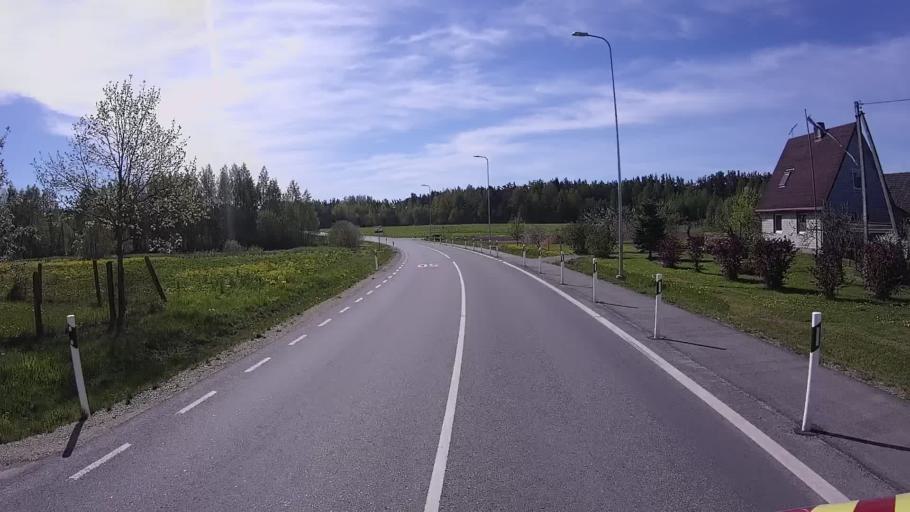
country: EE
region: Polvamaa
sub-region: Raepina vald
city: Rapina
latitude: 58.0000
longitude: 27.5447
